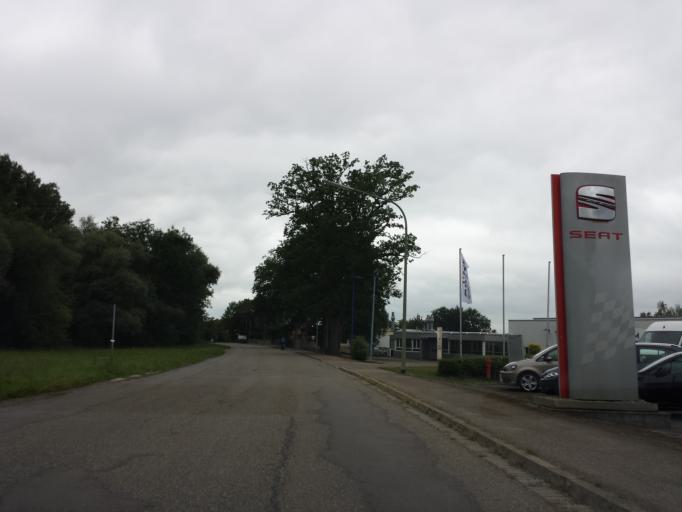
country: DE
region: Bavaria
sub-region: Swabia
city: Guenzburg
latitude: 48.4700
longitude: 10.2760
